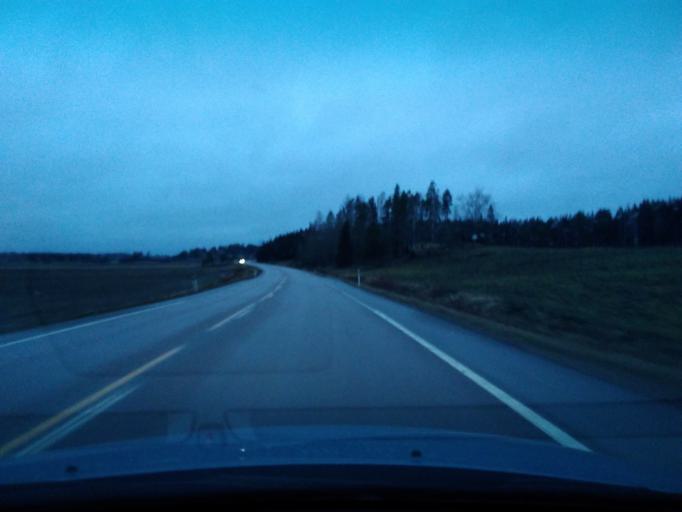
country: FI
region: Uusimaa
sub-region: Porvoo
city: Askola
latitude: 60.4822
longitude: 25.5630
